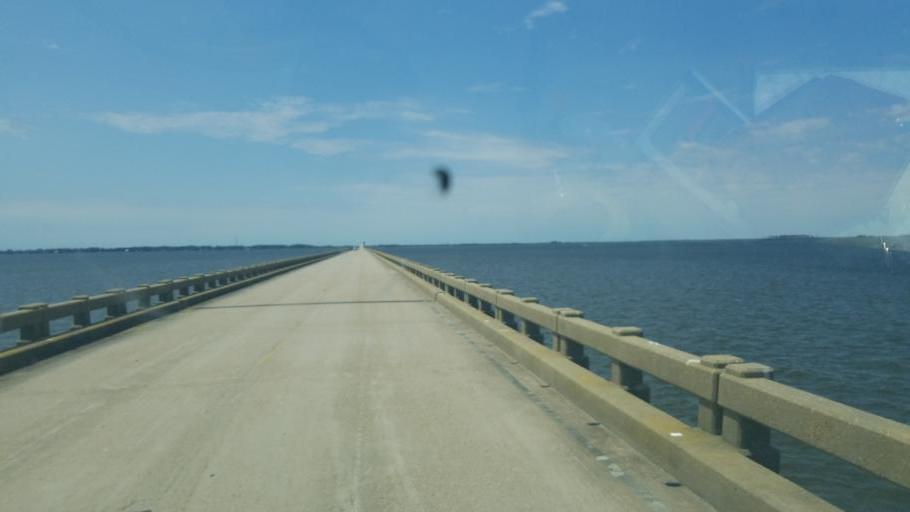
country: US
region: North Carolina
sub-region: Dare County
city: Manteo
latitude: 35.9248
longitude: -75.7309
